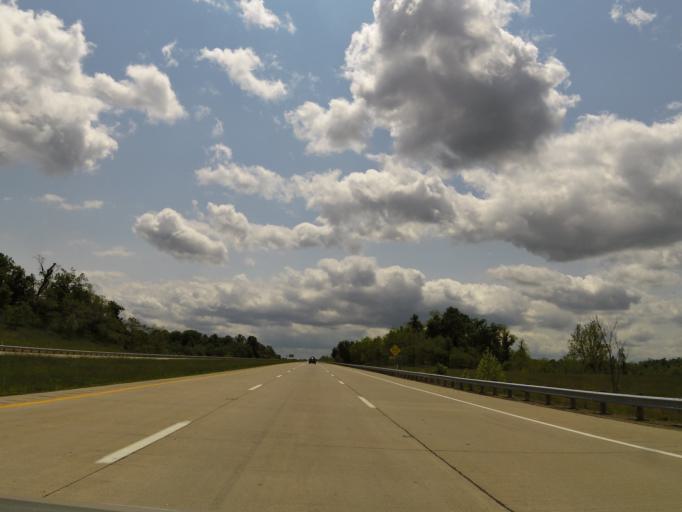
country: US
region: Ohio
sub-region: Athens County
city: Athens
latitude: 39.2876
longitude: -82.1023
